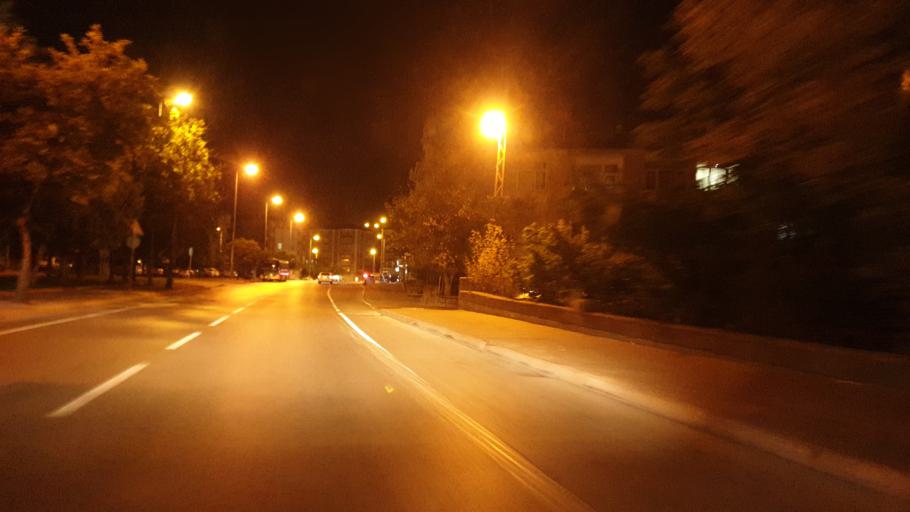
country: TR
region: Kayseri
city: Talas
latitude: 38.6960
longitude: 35.5455
